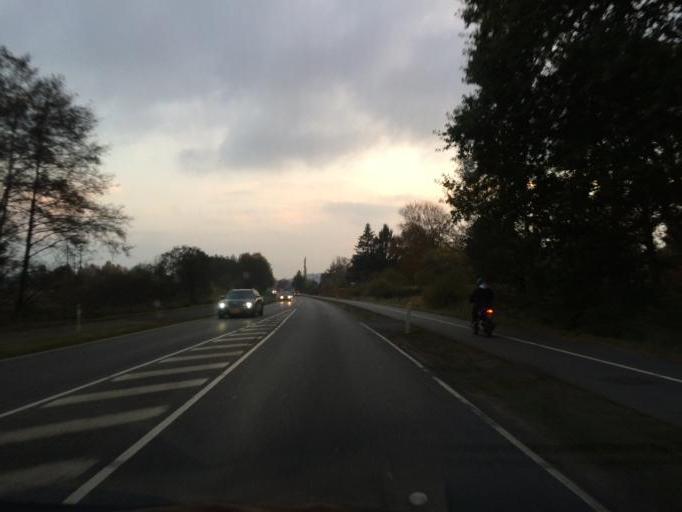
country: DK
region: Central Jutland
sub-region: Silkeborg Kommune
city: Silkeborg
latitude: 56.1684
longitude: 9.5141
